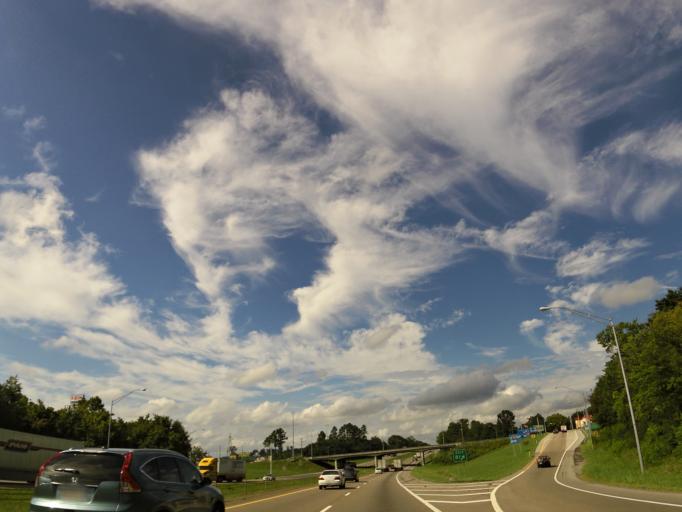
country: US
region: Tennessee
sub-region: Loudon County
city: Lenoir City
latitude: 35.8307
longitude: -84.2775
